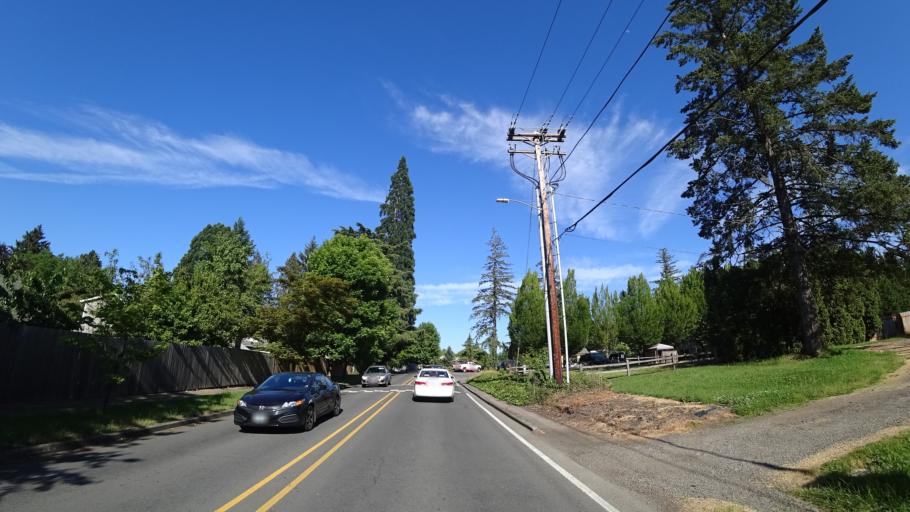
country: US
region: Oregon
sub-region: Washington County
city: Beaverton
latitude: 45.4665
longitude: -122.8064
